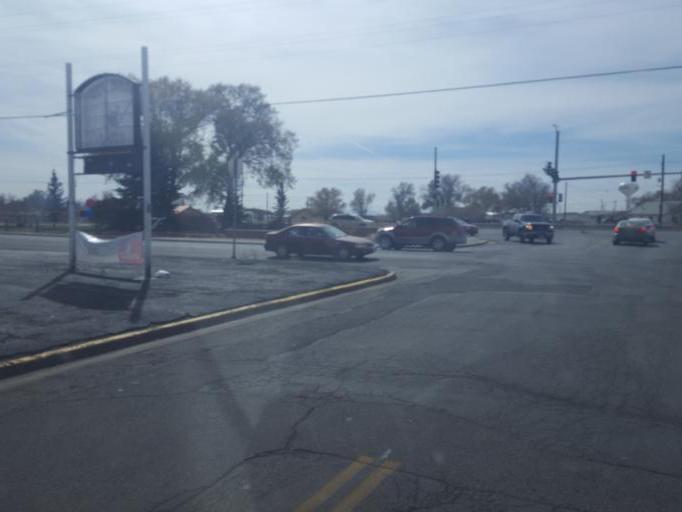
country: US
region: Colorado
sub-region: Alamosa County
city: Alamosa
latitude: 37.4734
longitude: -105.8887
